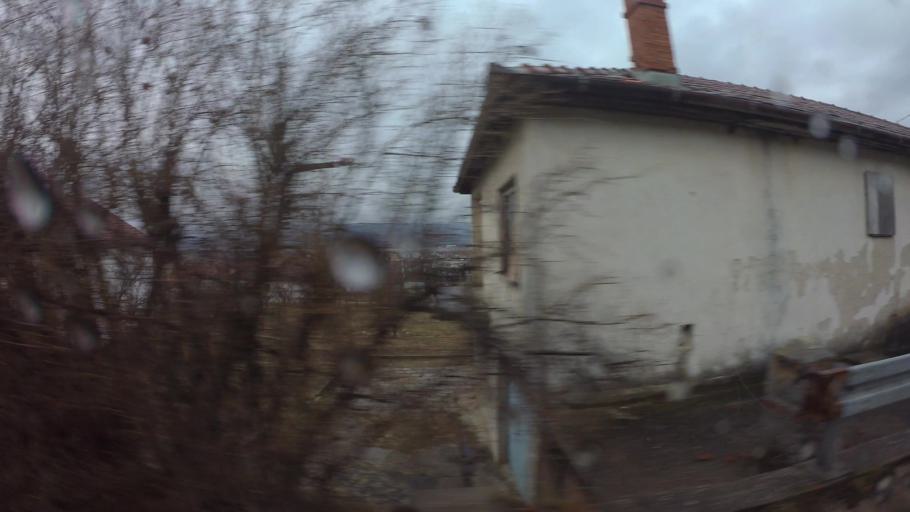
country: BA
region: Federation of Bosnia and Herzegovina
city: Blagaj
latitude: 43.2911
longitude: 17.8594
